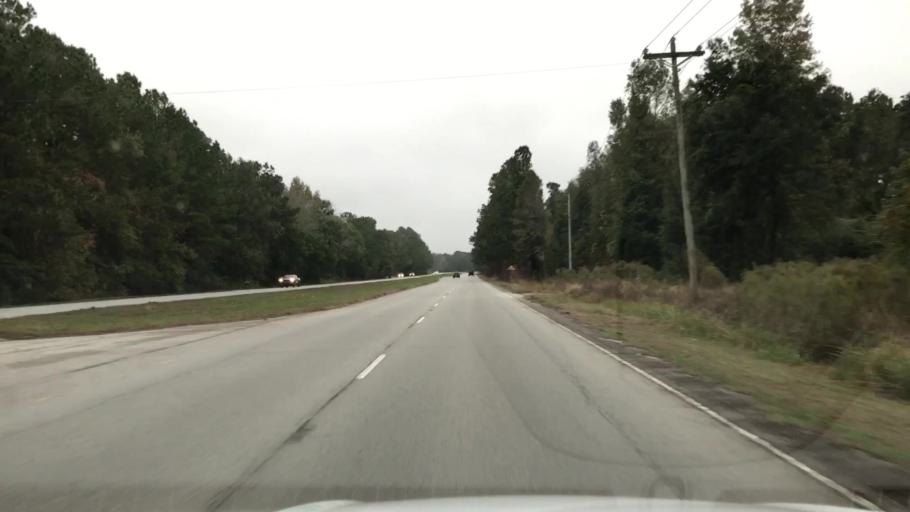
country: US
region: South Carolina
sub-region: Charleston County
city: Awendaw
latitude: 32.9953
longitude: -79.6448
